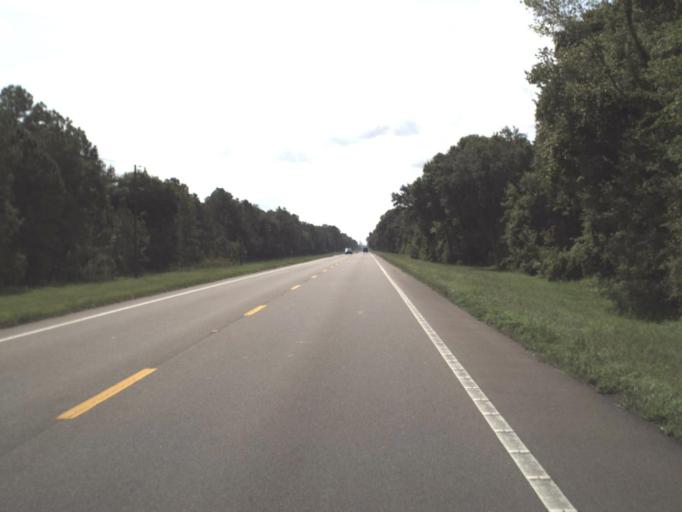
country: US
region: Florida
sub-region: Pasco County
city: Zephyrhills North
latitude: 28.2786
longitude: -82.1104
